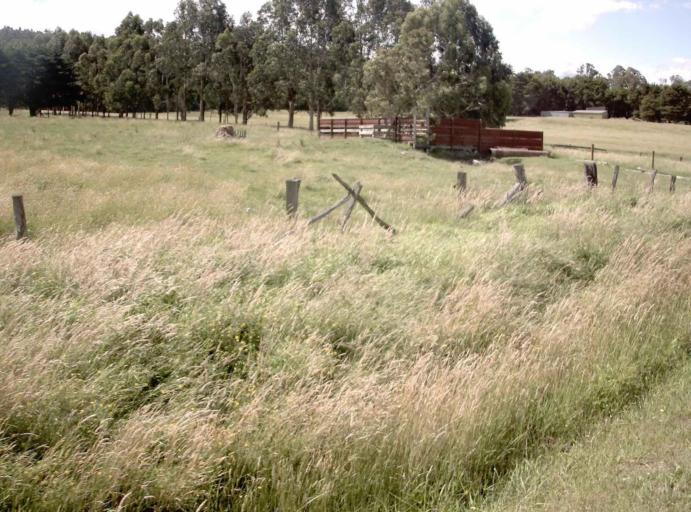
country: AU
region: Victoria
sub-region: Latrobe
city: Morwell
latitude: -38.1522
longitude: 146.4374
